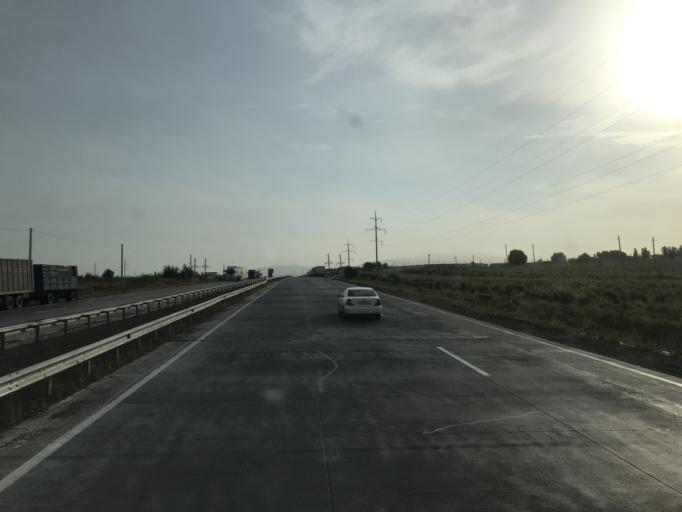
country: UZ
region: Toshkent
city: Qibray
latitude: 41.5233
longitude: 69.3965
